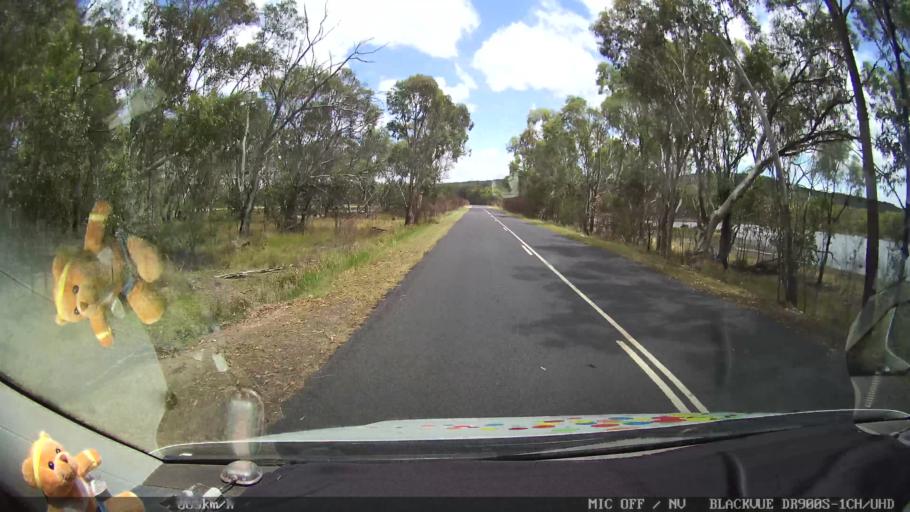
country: AU
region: New South Wales
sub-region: Glen Innes Severn
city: Glen Innes
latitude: -29.4643
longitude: 151.6194
